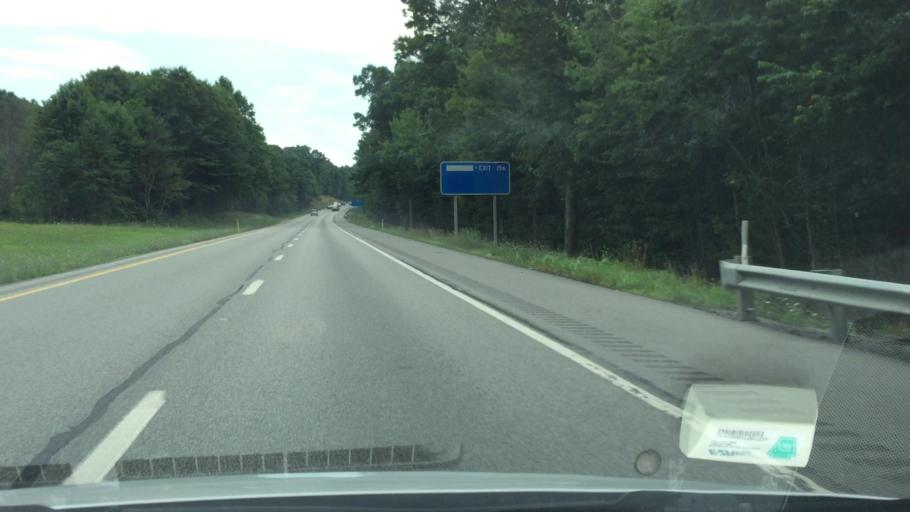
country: US
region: Pennsylvania
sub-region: Bedford County
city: Earlston
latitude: 39.9048
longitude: -78.2387
